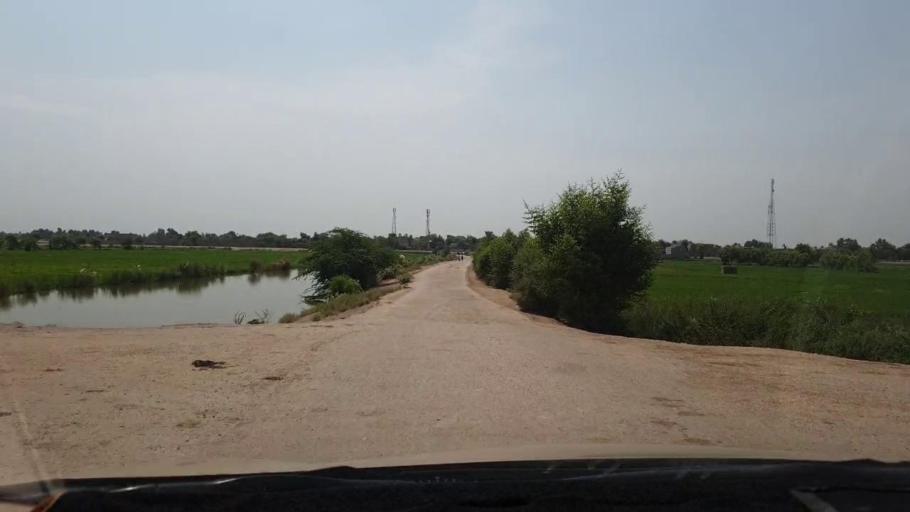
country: PK
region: Sindh
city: Larkana
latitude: 27.6235
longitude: 68.2752
